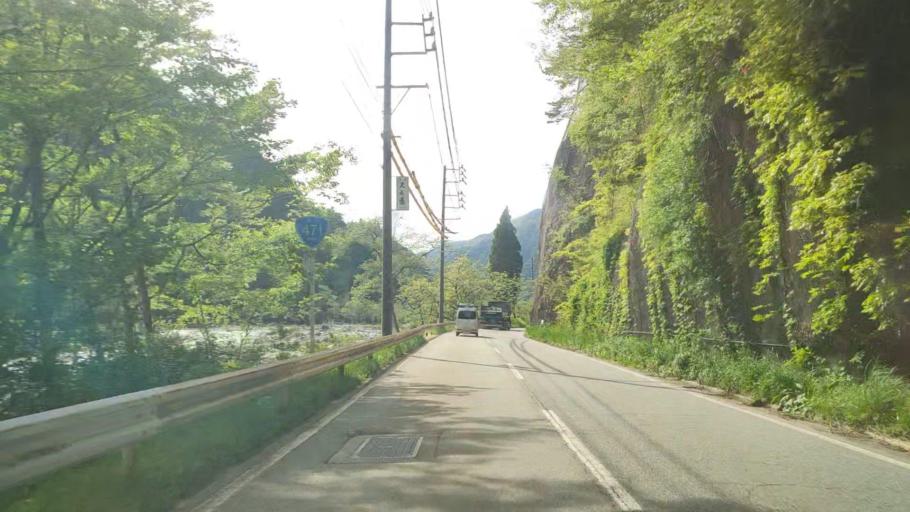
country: JP
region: Gifu
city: Takayama
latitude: 36.2516
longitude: 137.4797
